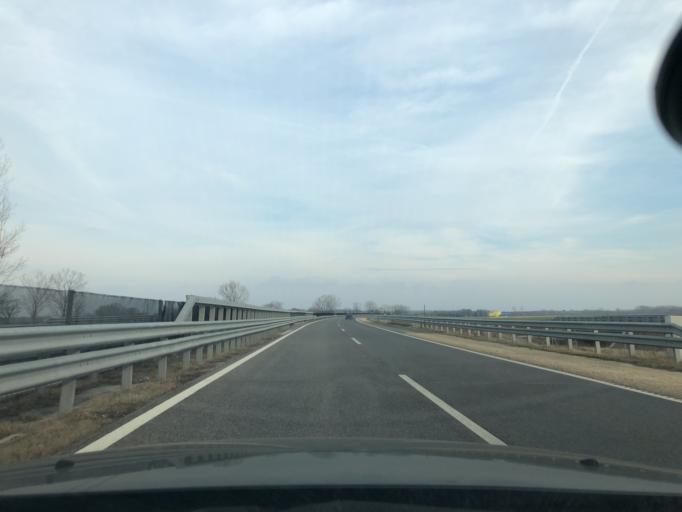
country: HU
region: Gyor-Moson-Sopron
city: Rabapatona
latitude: 47.6615
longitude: 17.4867
